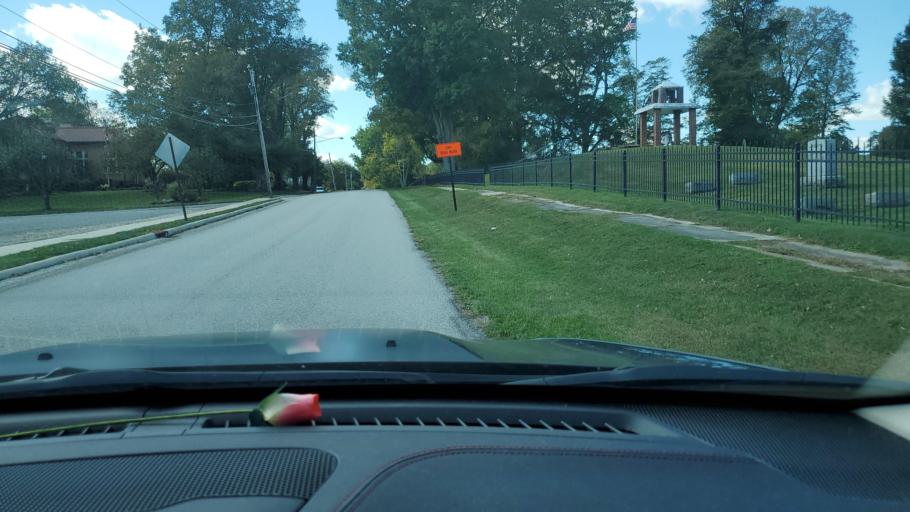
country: US
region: Ohio
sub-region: Ashtabula County
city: Andover
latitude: 41.4483
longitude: -80.5868
